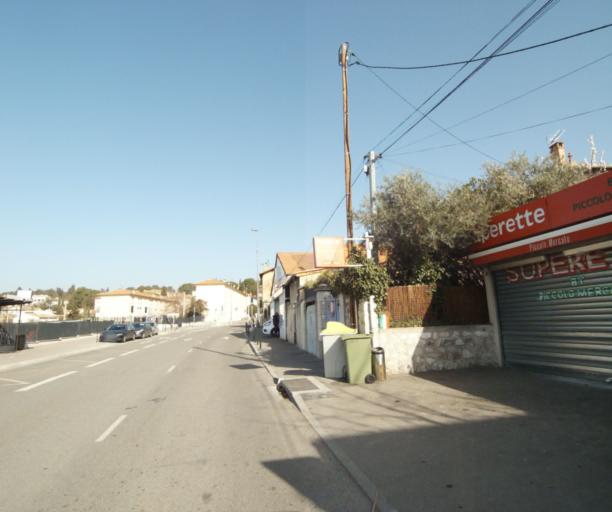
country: FR
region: Provence-Alpes-Cote d'Azur
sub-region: Departement des Bouches-du-Rhone
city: Aix-en-Provence
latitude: 43.5359
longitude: 5.4450
